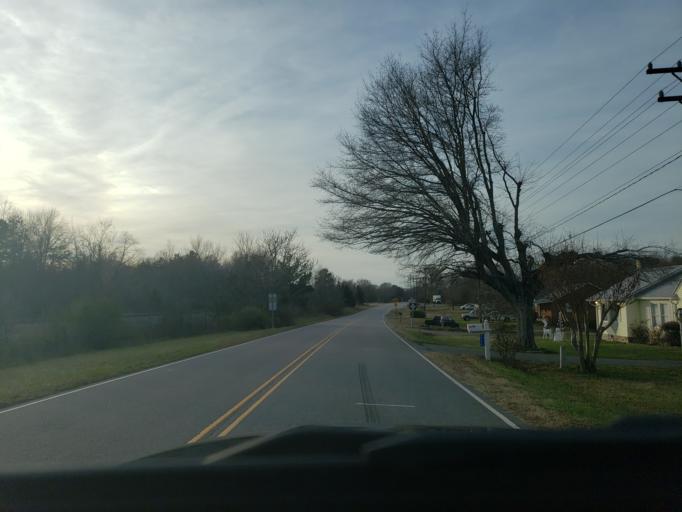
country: US
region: North Carolina
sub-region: Cleveland County
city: Boiling Springs
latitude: 35.3045
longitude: -81.7211
